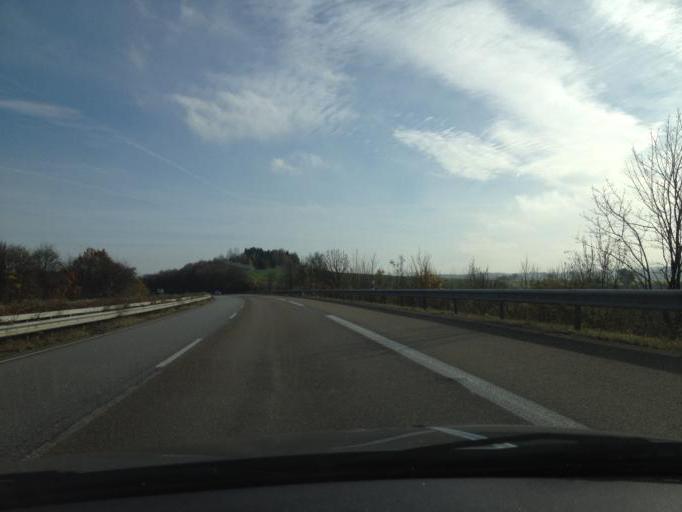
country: DE
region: Rheinland-Pfalz
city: Kleinsteinhausen
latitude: 49.2188
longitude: 7.4463
